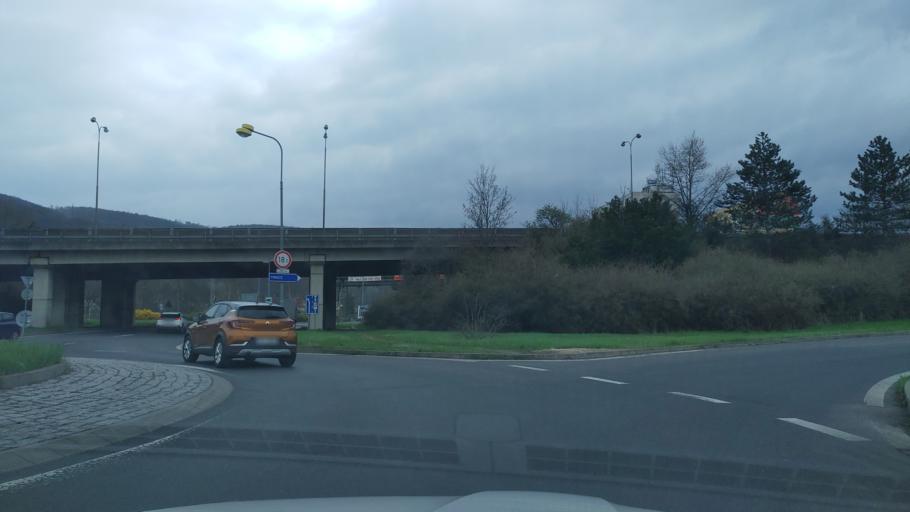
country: CZ
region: Ustecky
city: Trmice
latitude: 50.6486
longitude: 14.0054
